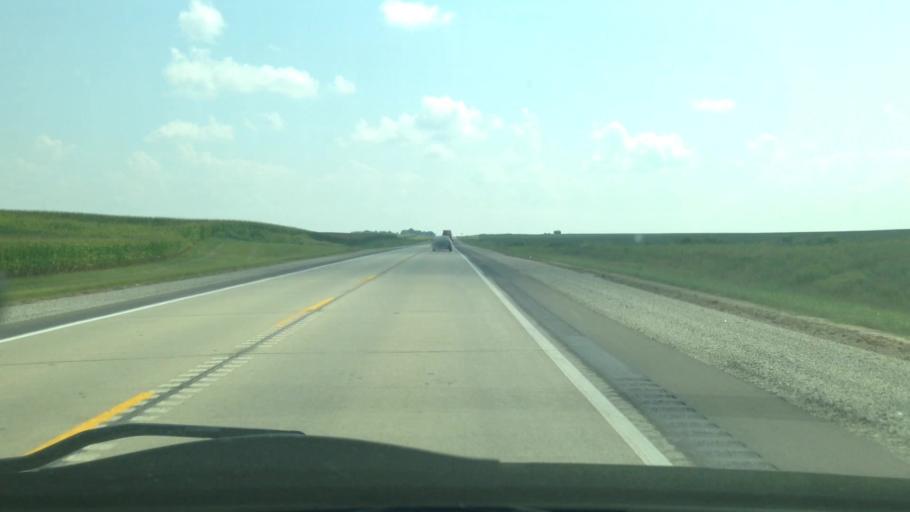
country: US
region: Iowa
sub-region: Howard County
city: Cresco
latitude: 43.4376
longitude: -92.2986
